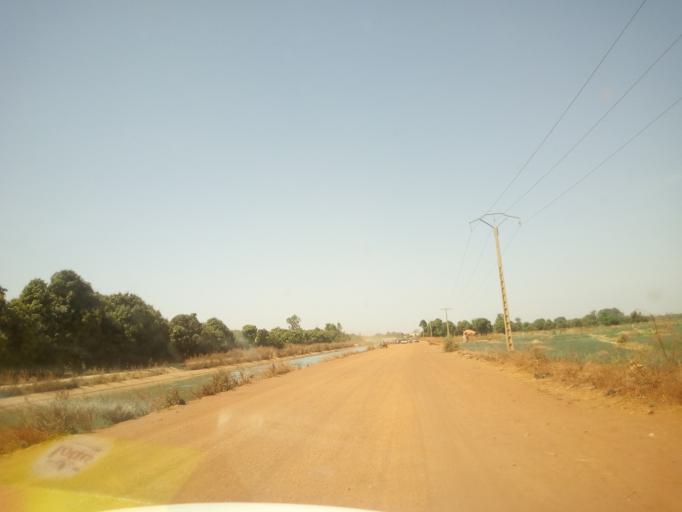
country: ML
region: Bamako
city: Bamako
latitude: 12.6207
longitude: -7.7678
